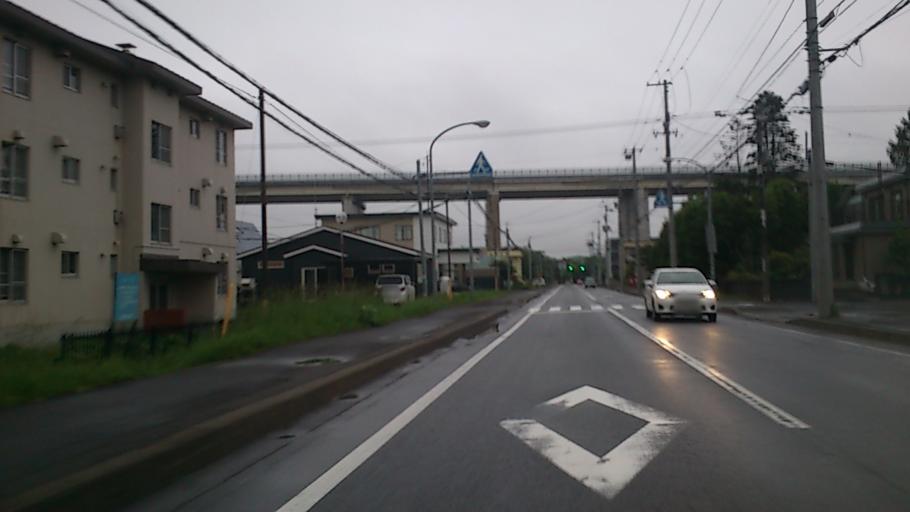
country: JP
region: Hokkaido
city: Chitose
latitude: 42.8179
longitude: 141.6214
